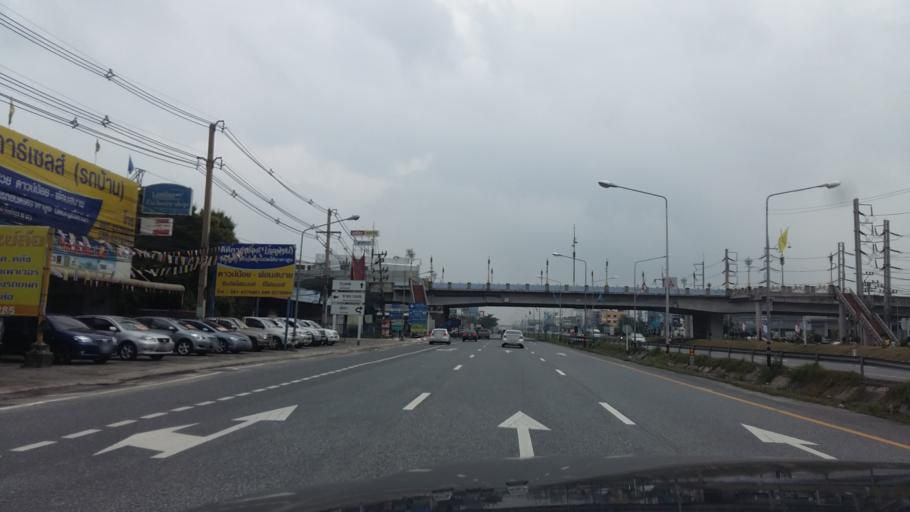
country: TH
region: Chon Buri
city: Chon Buri
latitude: 13.2932
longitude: 100.9434
